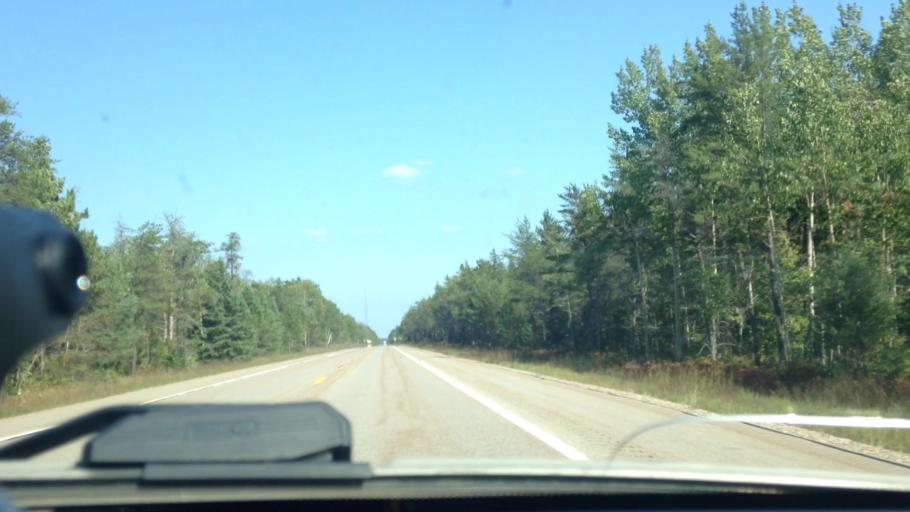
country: US
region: Michigan
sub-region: Chippewa County
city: Sault Ste. Marie
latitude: 46.3679
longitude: -84.7464
